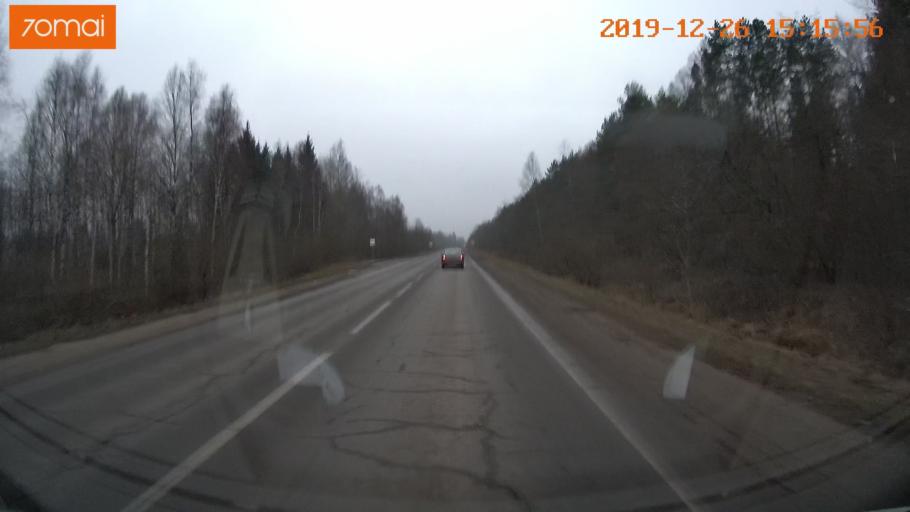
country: RU
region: Jaroslavl
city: Rybinsk
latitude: 58.0918
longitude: 38.8725
